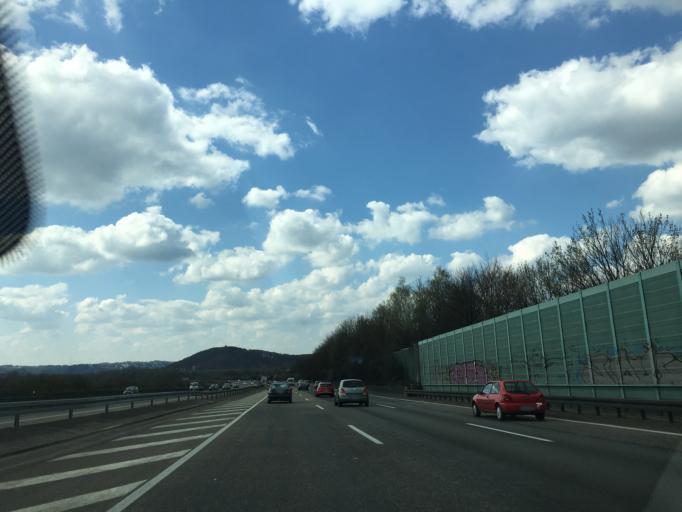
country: DE
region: North Rhine-Westphalia
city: Herdecke
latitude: 51.3994
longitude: 7.4568
